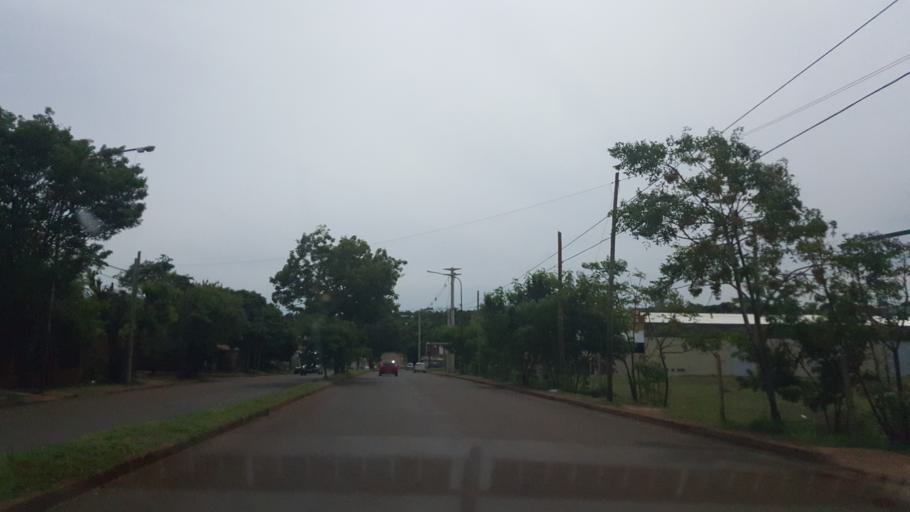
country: AR
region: Misiones
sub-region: Departamento de Capital
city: Posadas
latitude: -27.3914
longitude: -55.9427
